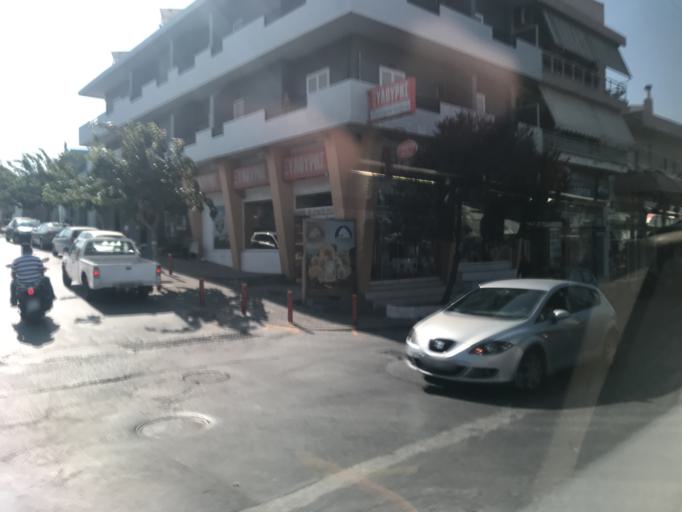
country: GR
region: Crete
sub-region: Nomos Irakleiou
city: Irakleion
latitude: 35.3330
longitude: 25.1143
